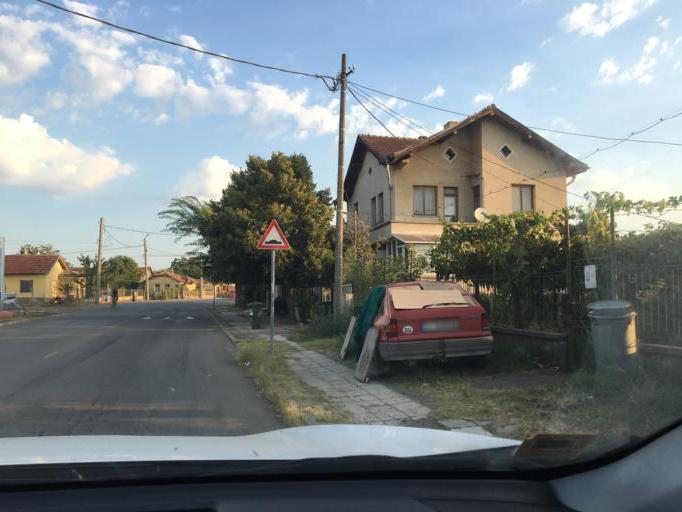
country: BG
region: Burgas
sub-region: Obshtina Burgas
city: Burgas
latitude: 42.6118
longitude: 27.4932
